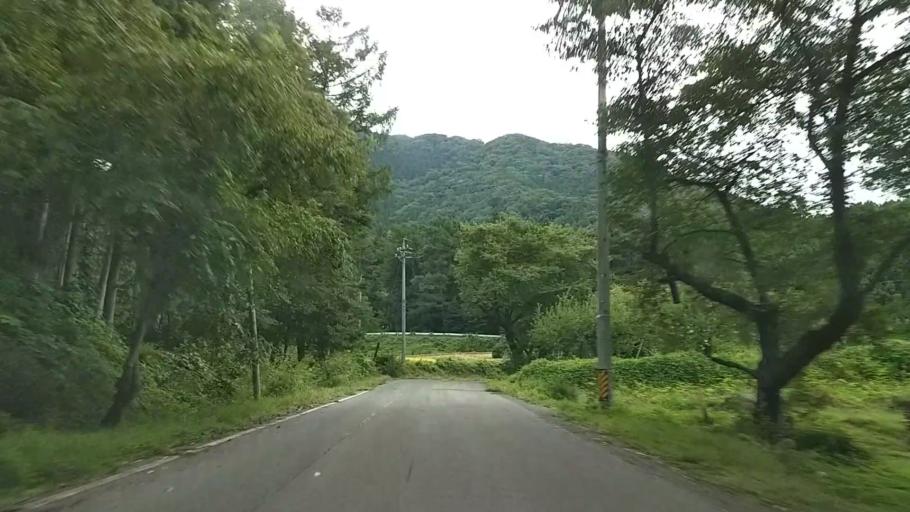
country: JP
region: Nagano
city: Iiyama
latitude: 36.8165
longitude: 138.3689
